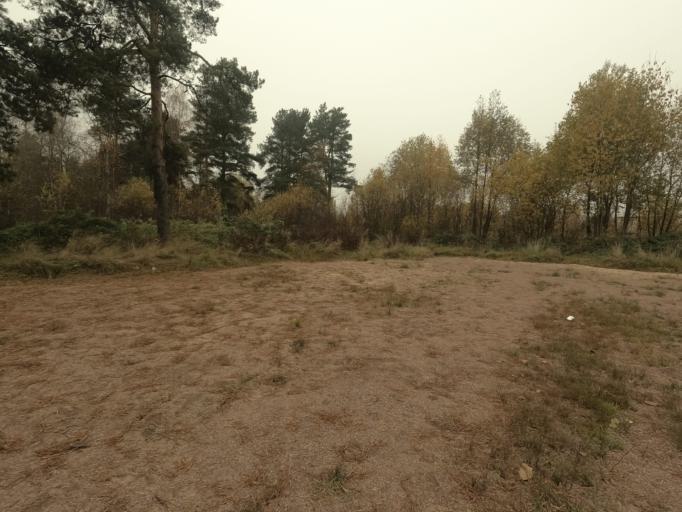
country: RU
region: Leningrad
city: Pavlovo
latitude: 59.7654
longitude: 30.9604
